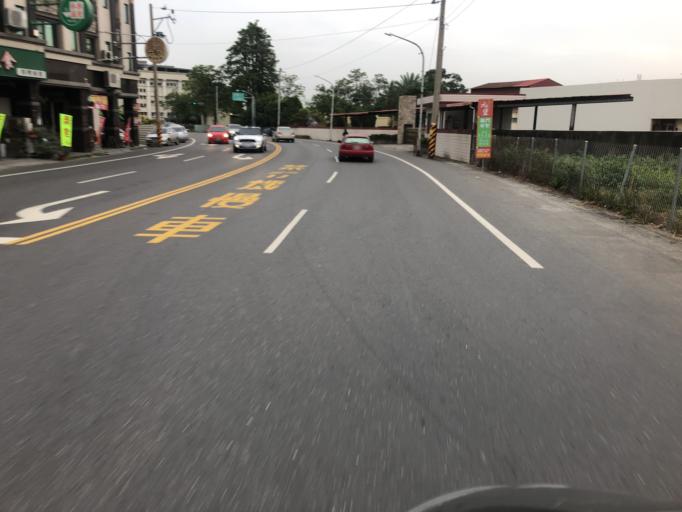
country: TW
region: Taiwan
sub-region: Tainan
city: Tainan
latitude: 23.1276
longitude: 120.2874
